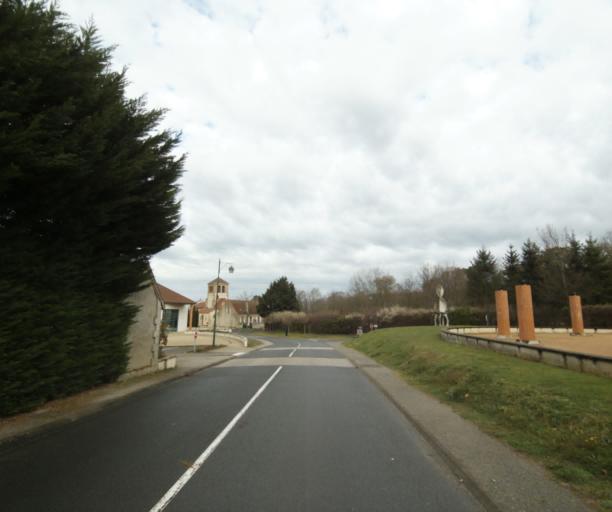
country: FR
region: Auvergne
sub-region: Departement de l'Allier
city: Toulon-sur-Allier
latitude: 46.5183
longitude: 3.3612
